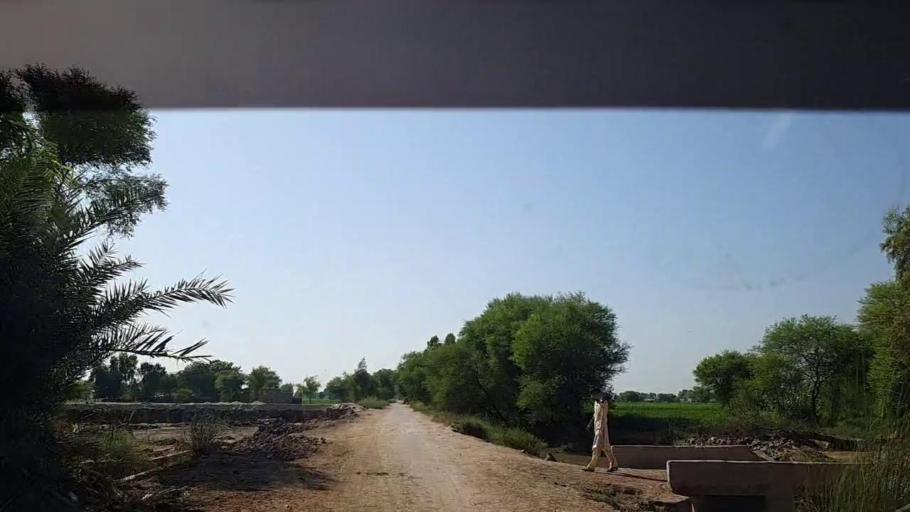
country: PK
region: Sindh
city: Ghauspur
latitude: 28.1730
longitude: 69.0558
